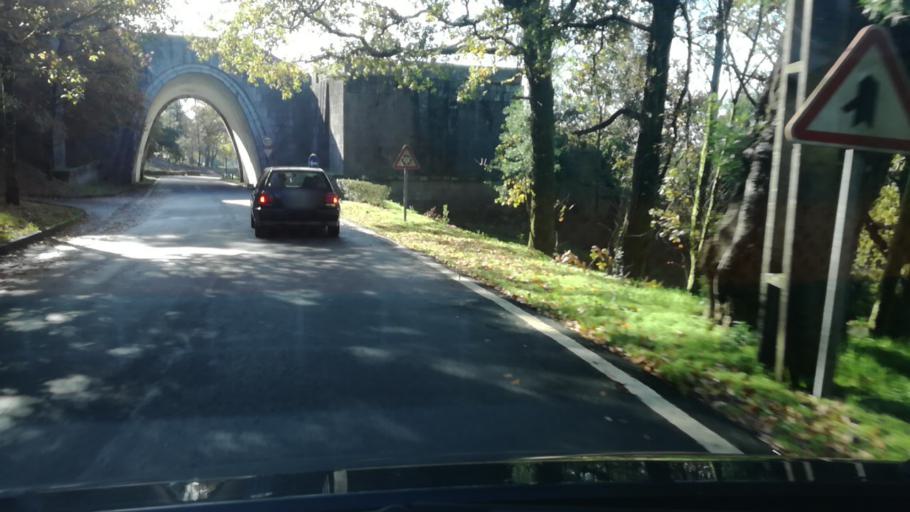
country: PT
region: Braga
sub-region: Braga
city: Braga
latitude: 41.5428
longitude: -8.3720
